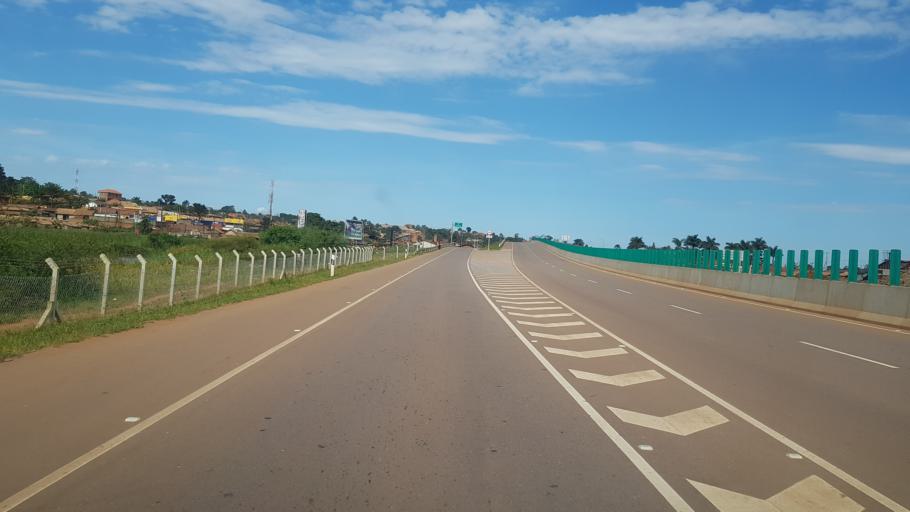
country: UG
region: Central Region
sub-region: Wakiso District
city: Kajansi
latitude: 0.2140
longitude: 32.5392
